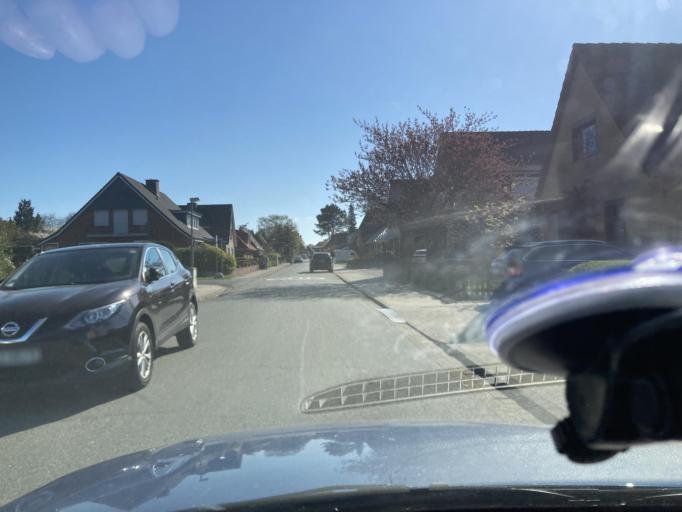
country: DE
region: Schleswig-Holstein
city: Wesseln
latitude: 54.1903
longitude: 9.0843
